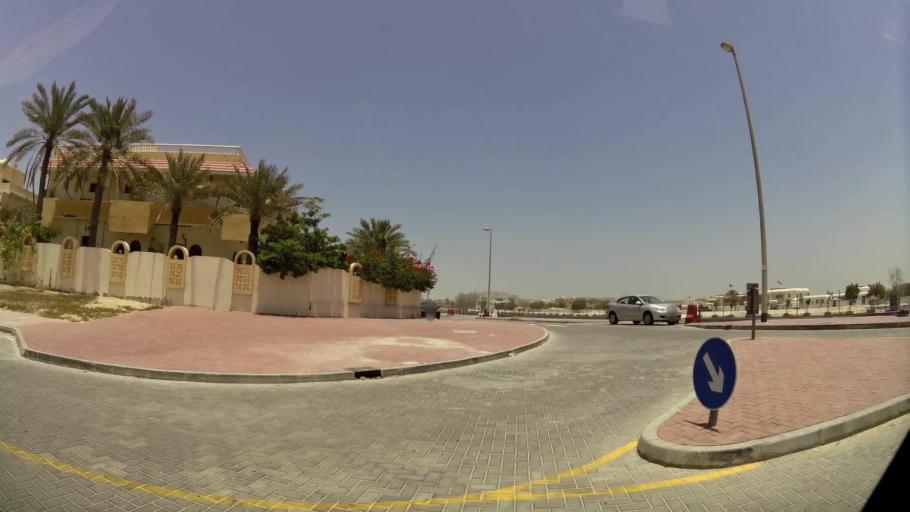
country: AE
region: Dubai
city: Dubai
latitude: 25.1927
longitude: 55.2408
